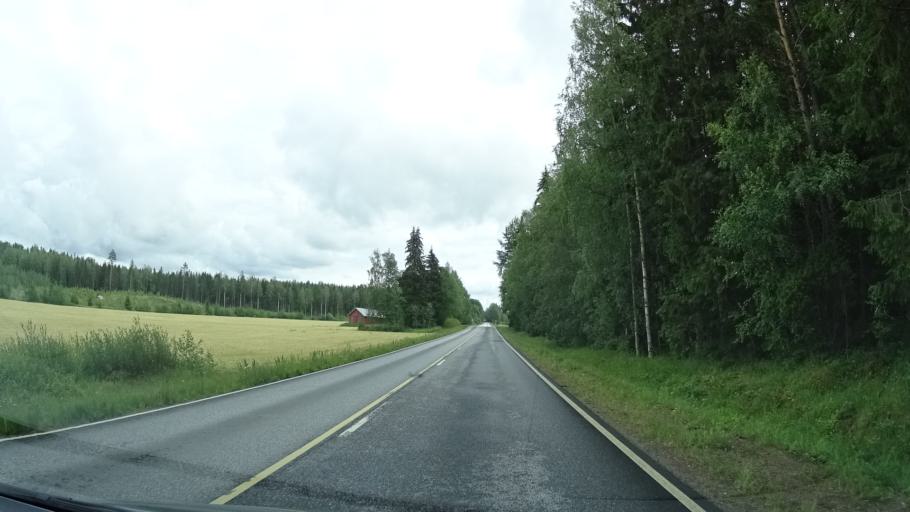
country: FI
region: Haeme
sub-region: Forssa
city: Humppila
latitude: 61.0960
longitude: 23.3586
